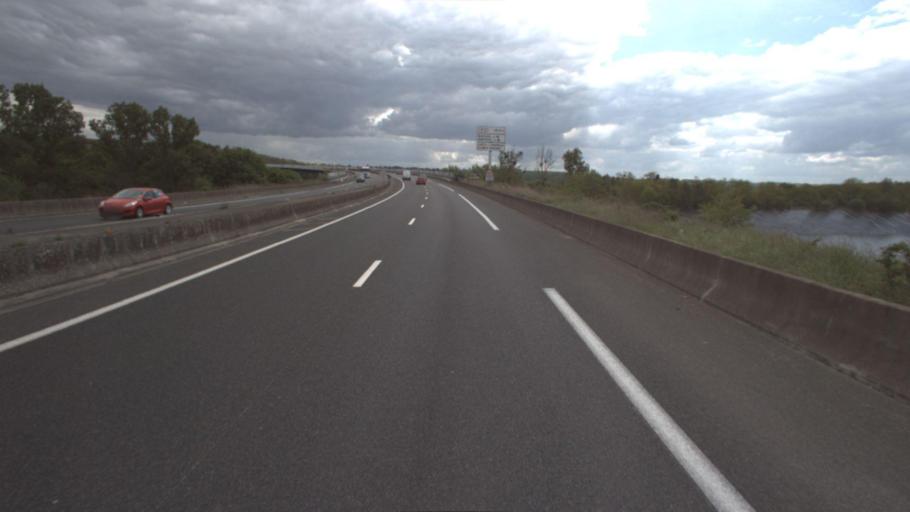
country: FR
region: Ile-de-France
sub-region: Departement de Seine-et-Marne
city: Mareuil-les-Meaux
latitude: 48.9228
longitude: 2.8453
